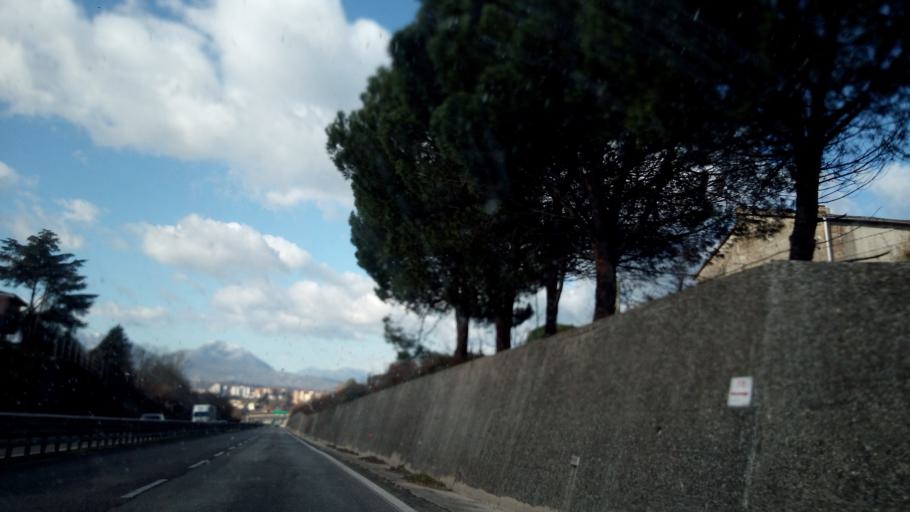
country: IT
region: Campania
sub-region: Provincia di Benevento
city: Maccoli-Perrillo
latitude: 41.1149
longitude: 14.8162
